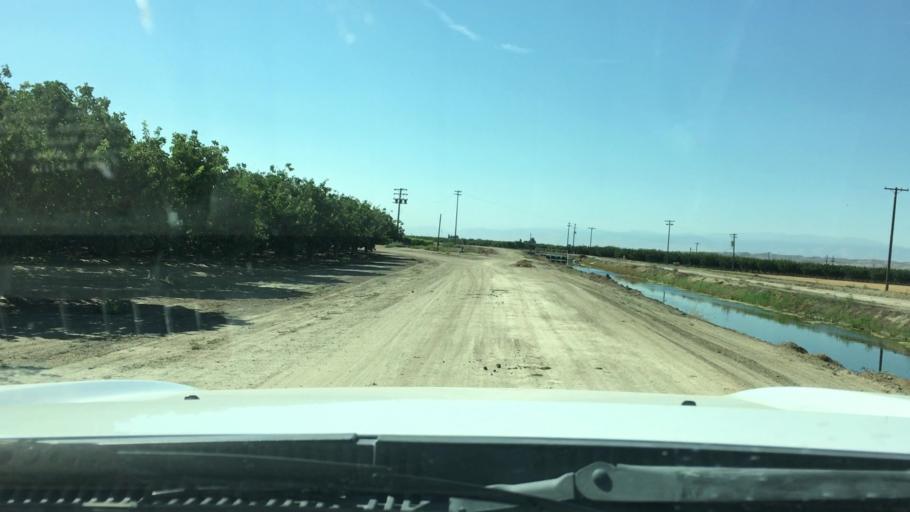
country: US
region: California
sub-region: Kern County
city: Buttonwillow
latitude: 35.3668
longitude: -119.3966
